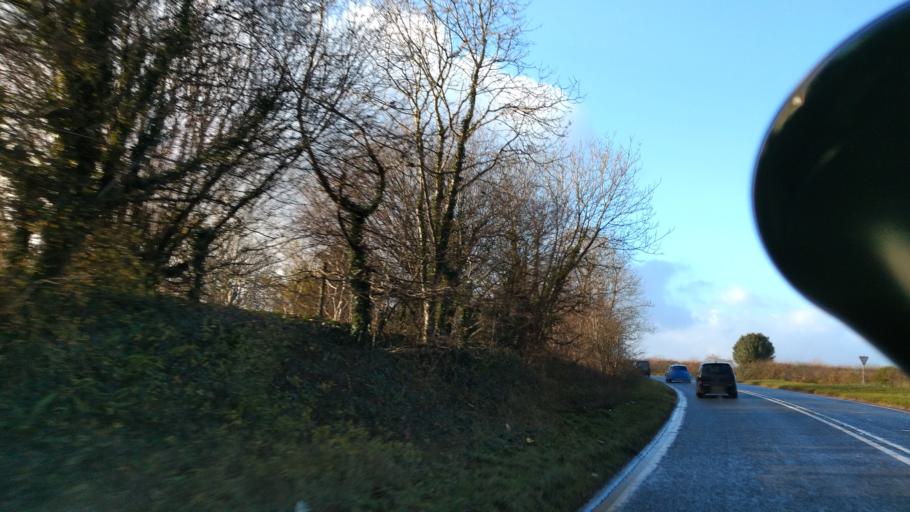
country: GB
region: England
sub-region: Somerset
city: Frome
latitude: 51.2038
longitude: -2.3977
